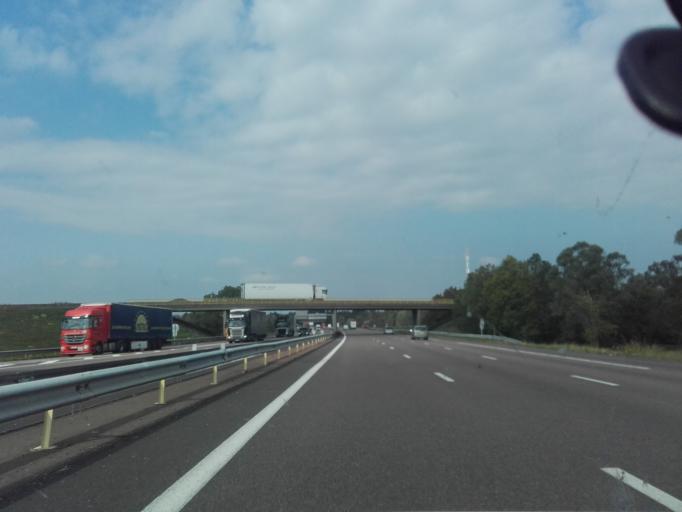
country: FR
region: Bourgogne
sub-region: Departement de Saone-et-Loire
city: Sevrey
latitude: 46.7496
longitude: 4.8323
